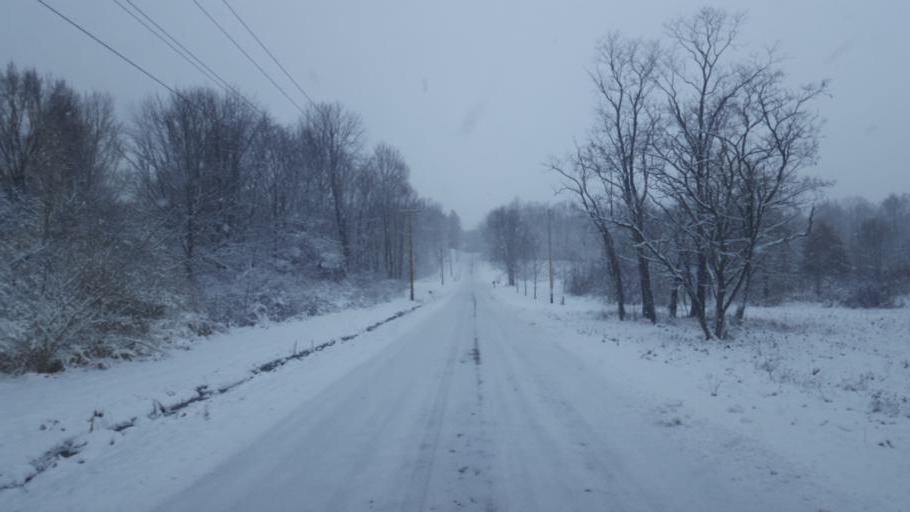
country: US
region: Ohio
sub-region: Knox County
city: Fredericktown
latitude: 40.4787
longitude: -82.6461
